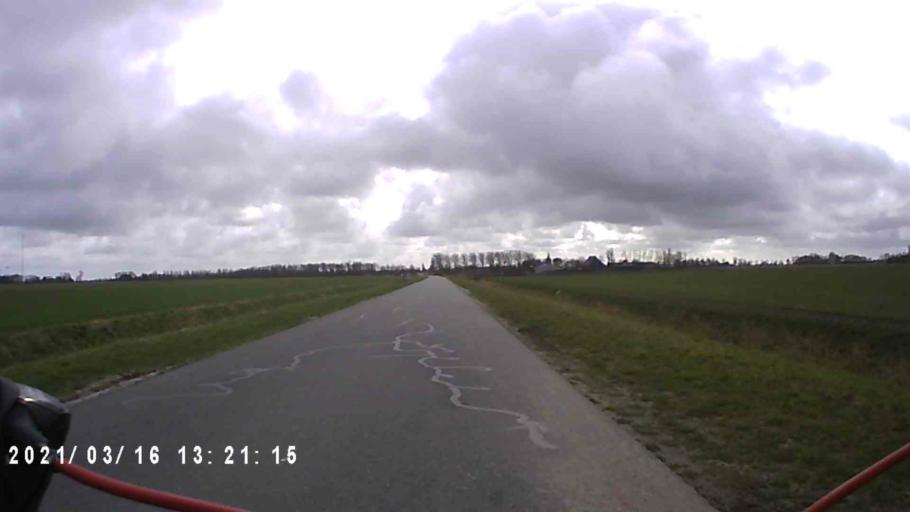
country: NL
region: Friesland
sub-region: Gemeente Het Bildt
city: Minnertsga
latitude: 53.2294
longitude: 5.5849
